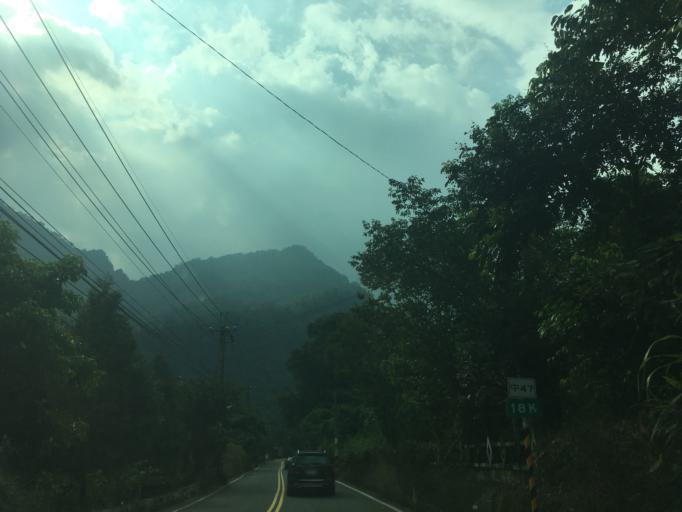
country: TW
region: Taiwan
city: Fengyuan
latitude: 24.3203
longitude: 120.9232
